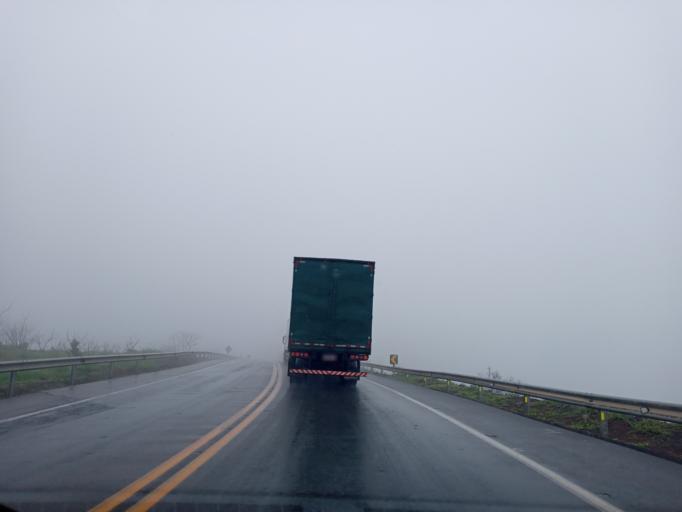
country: BR
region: Minas Gerais
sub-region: Luz
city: Luz
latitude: -19.7116
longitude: -45.9112
